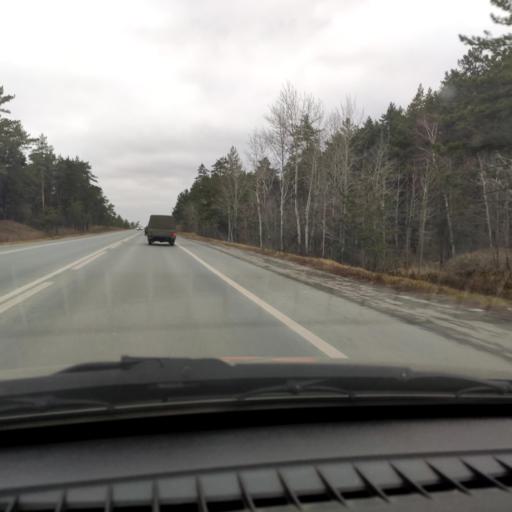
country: RU
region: Samara
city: Volzhskiy
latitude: 53.4410
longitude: 50.1064
